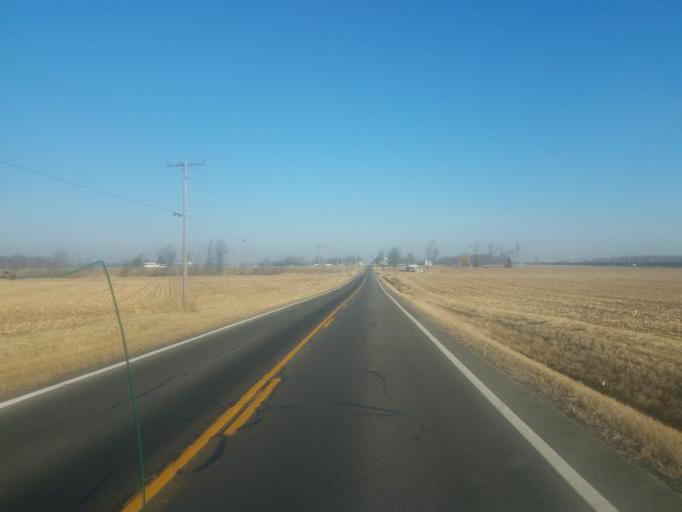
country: US
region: Ohio
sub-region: Crawford County
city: Bucyrus
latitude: 40.9886
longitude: -82.9253
